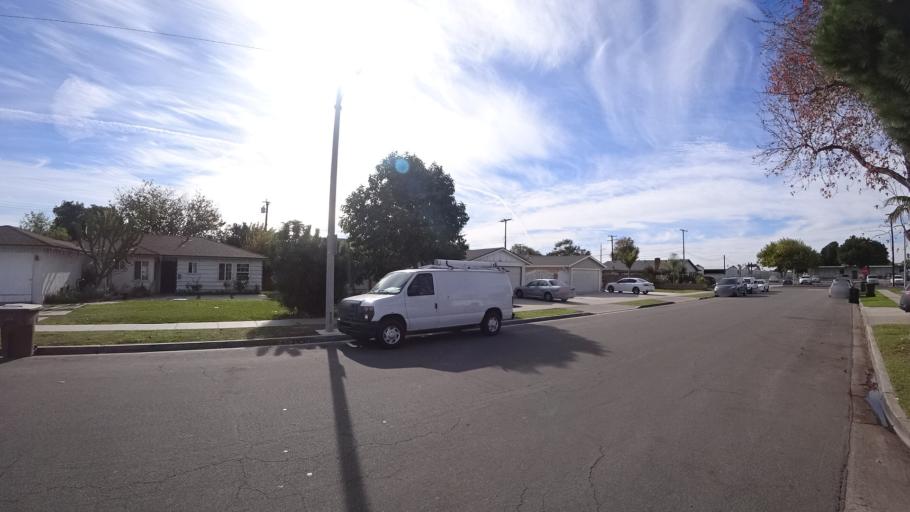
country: US
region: California
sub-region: Orange County
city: Garden Grove
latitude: 33.7658
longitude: -117.9108
